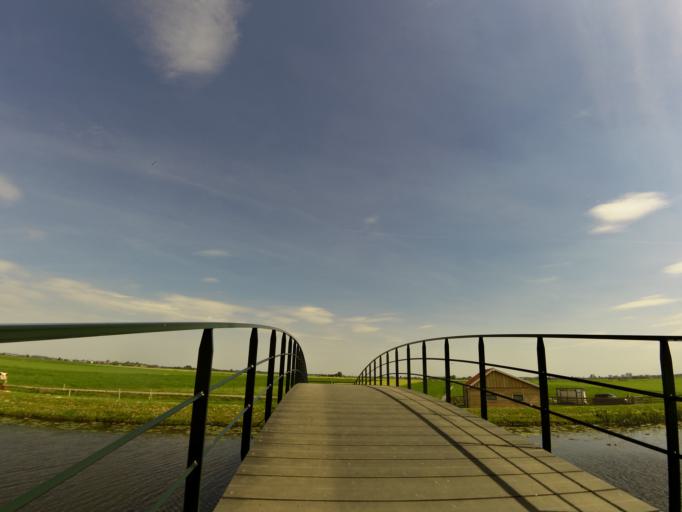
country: NL
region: South Holland
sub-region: Gemeente Rijnwoude
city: Benthuizen
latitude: 52.1048
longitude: 4.5176
